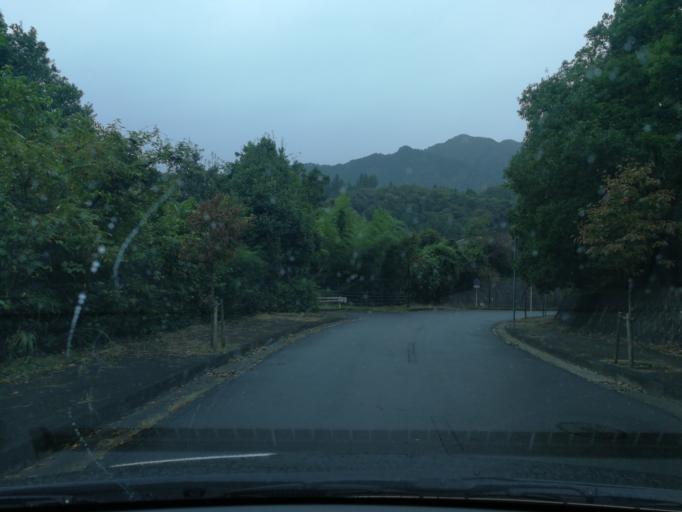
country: JP
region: Yamanashi
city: Uenohara
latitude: 35.6016
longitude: 139.2116
